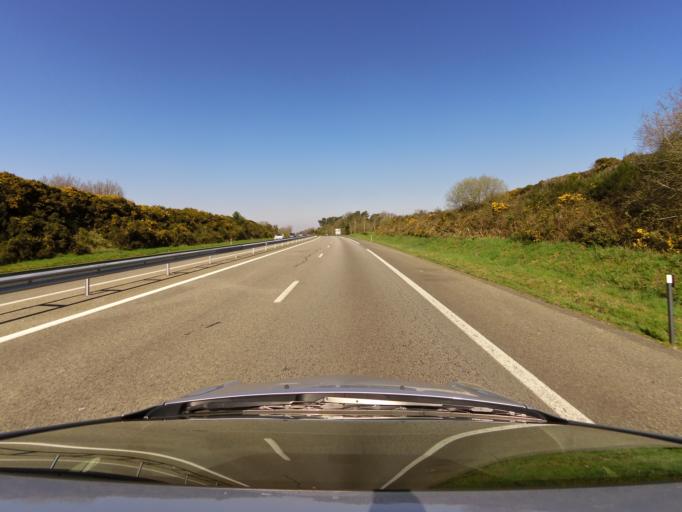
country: FR
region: Brittany
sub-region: Departement du Morbihan
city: Augan
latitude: 47.9377
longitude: -2.2573
